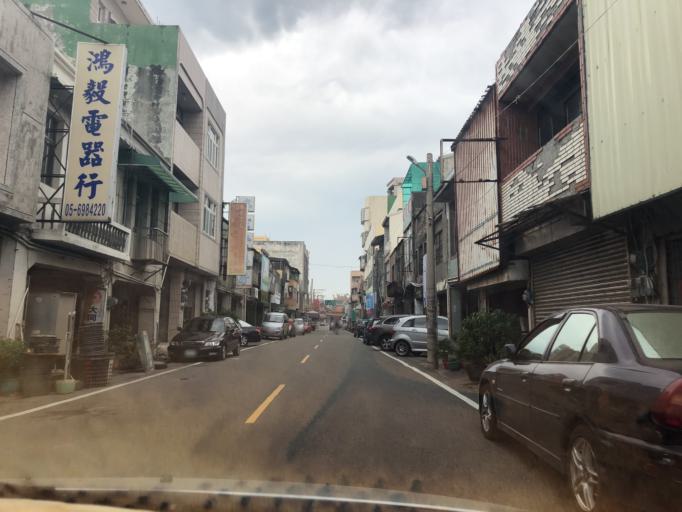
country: TW
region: Taiwan
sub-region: Chiayi
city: Taibao
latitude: 23.7004
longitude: 120.1975
